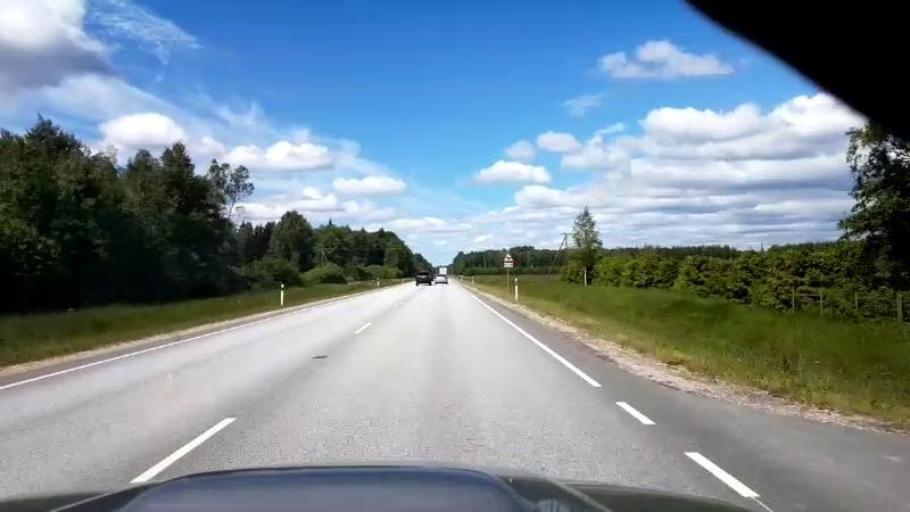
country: EE
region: Paernumaa
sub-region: Halinga vald
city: Parnu-Jaagupi
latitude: 58.5391
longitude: 24.5457
